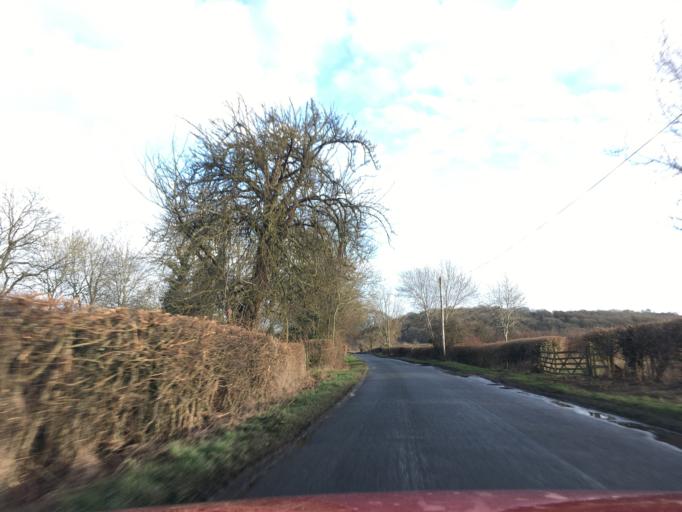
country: GB
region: England
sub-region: Warwickshire
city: Alcester
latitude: 52.2242
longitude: -1.8096
